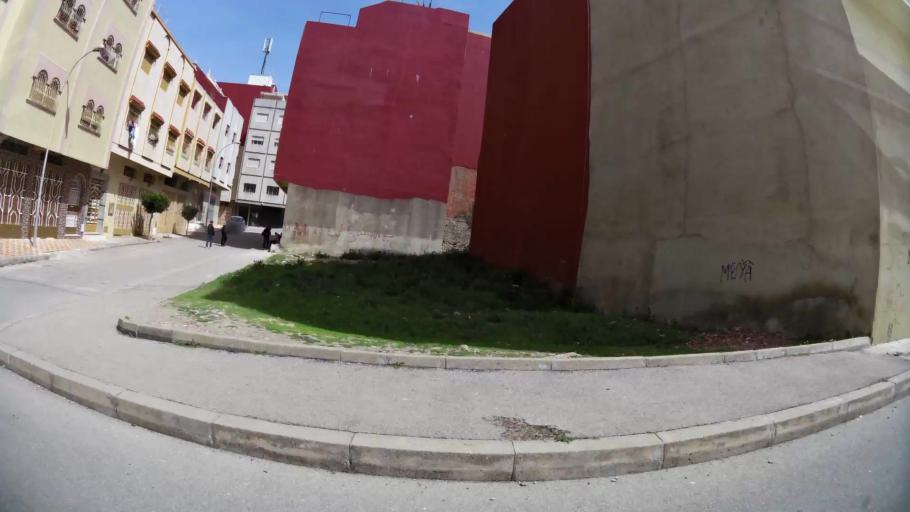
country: MA
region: Tanger-Tetouan
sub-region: Tanger-Assilah
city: Tangier
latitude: 35.7485
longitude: -5.8329
